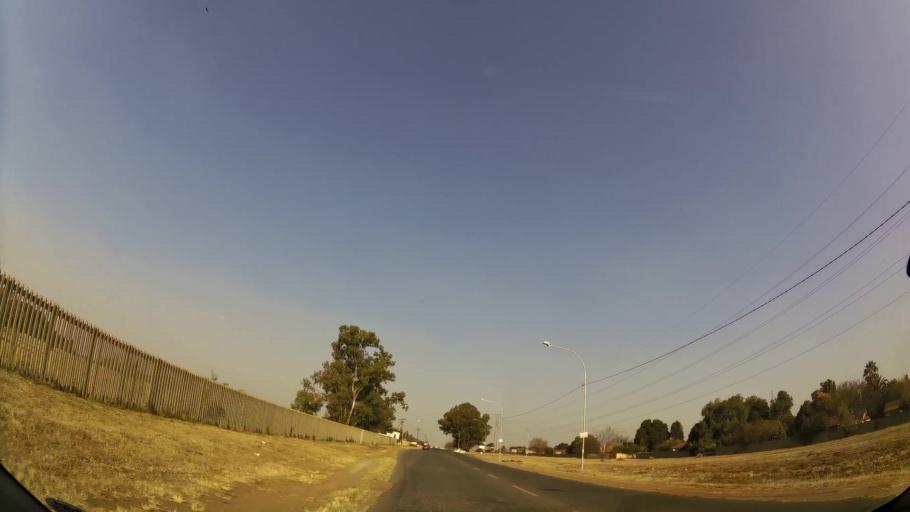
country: ZA
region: Gauteng
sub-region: Ekurhuleni Metropolitan Municipality
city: Benoni
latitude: -26.1184
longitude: 28.3774
